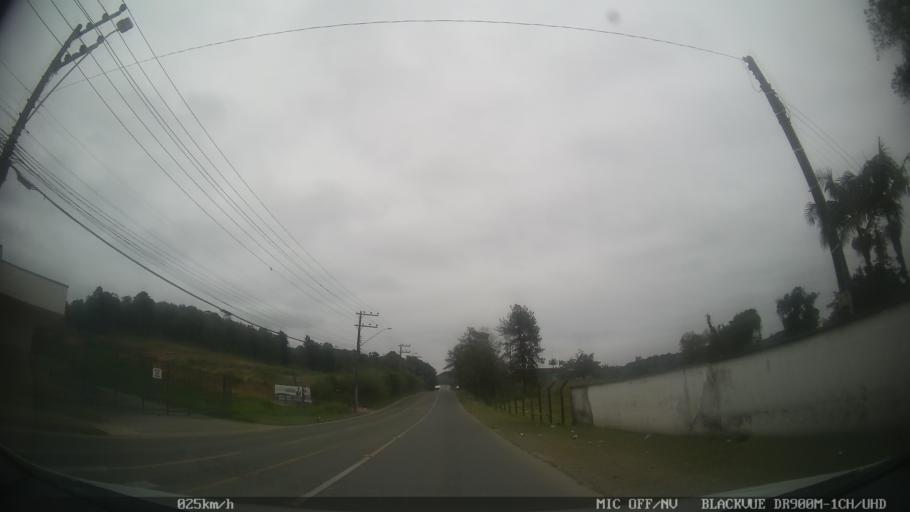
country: BR
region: Santa Catarina
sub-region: Joinville
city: Joinville
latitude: -26.3718
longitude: -48.8453
